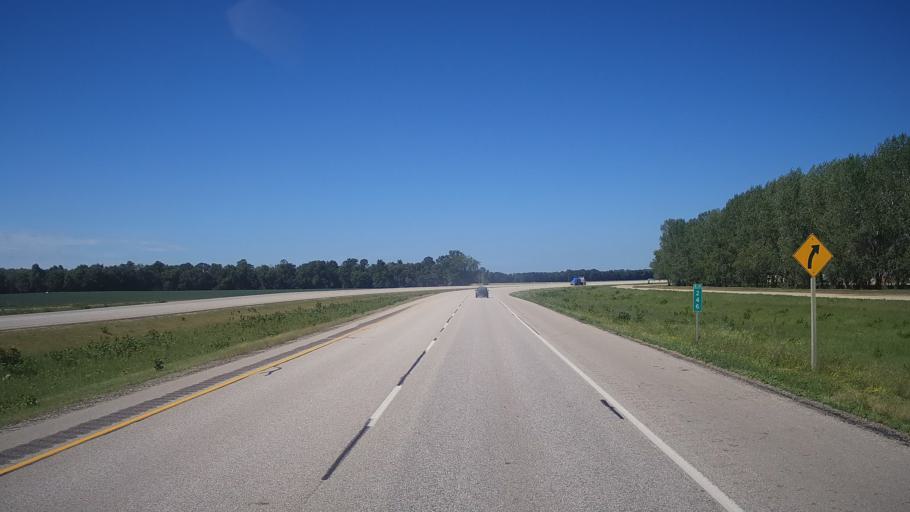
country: CA
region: Manitoba
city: Portage la Prairie
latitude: 49.9476
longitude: -98.2917
